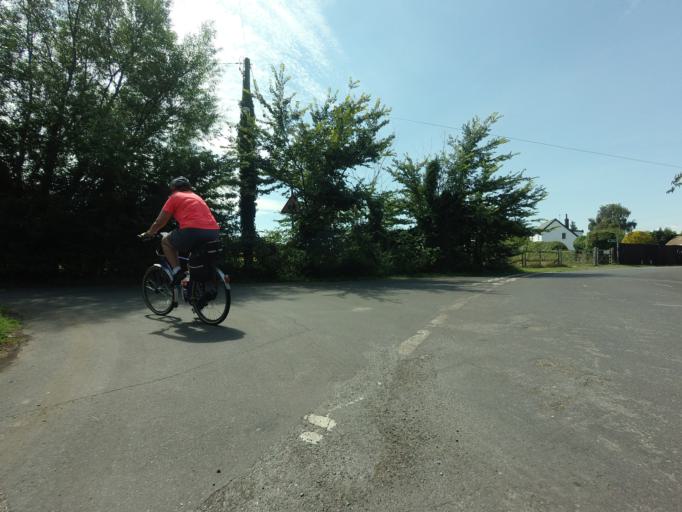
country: GB
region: England
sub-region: Kent
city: Stone
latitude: 50.9967
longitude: 0.8329
